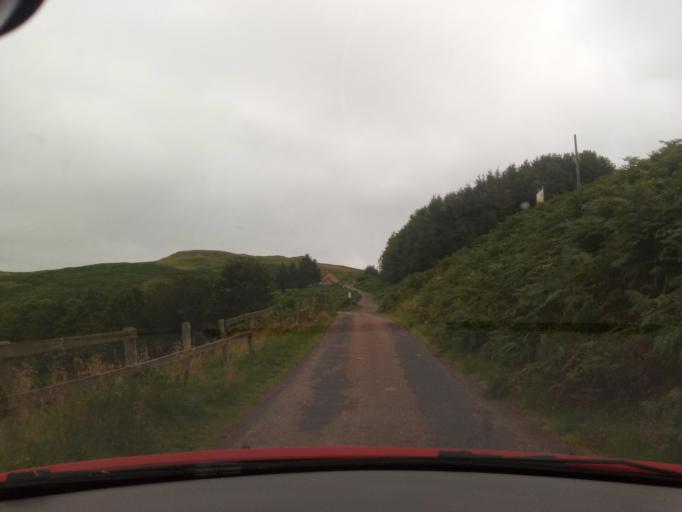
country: GB
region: England
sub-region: Northumberland
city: Rochester
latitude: 55.3708
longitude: -2.2152
